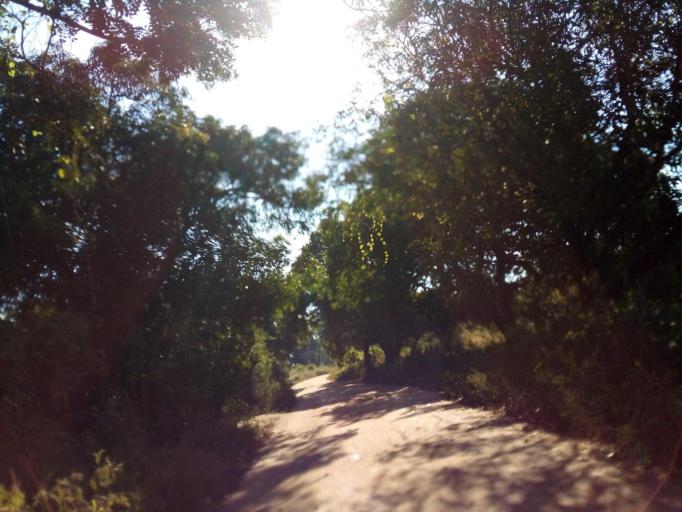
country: MZ
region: Zambezia
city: Quelimane
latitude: -17.5169
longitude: 36.6076
